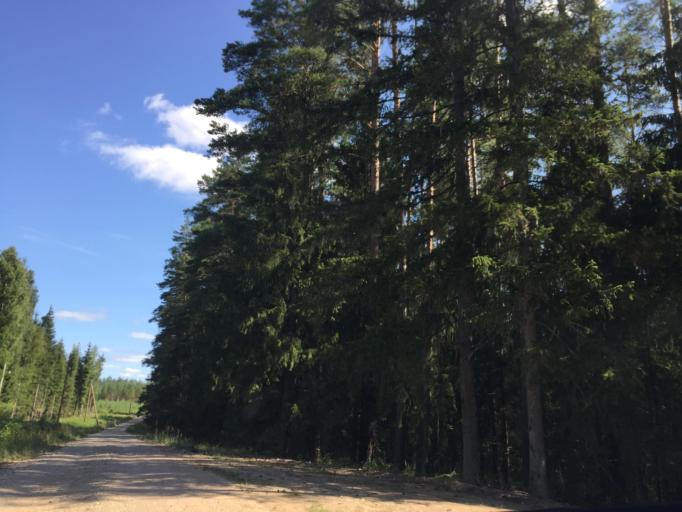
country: LV
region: Talsu Rajons
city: Stende
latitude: 57.1706
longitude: 22.3013
